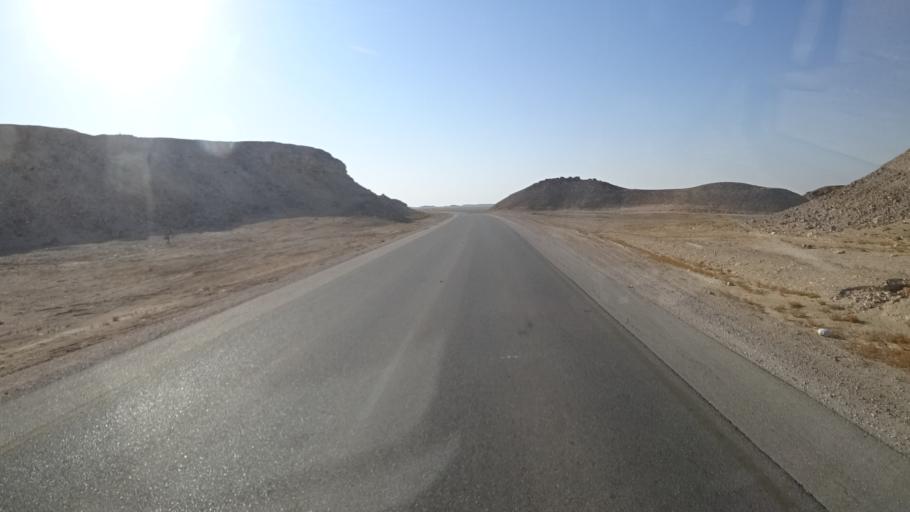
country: OM
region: Zufar
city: Salalah
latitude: 17.6423
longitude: 53.8550
